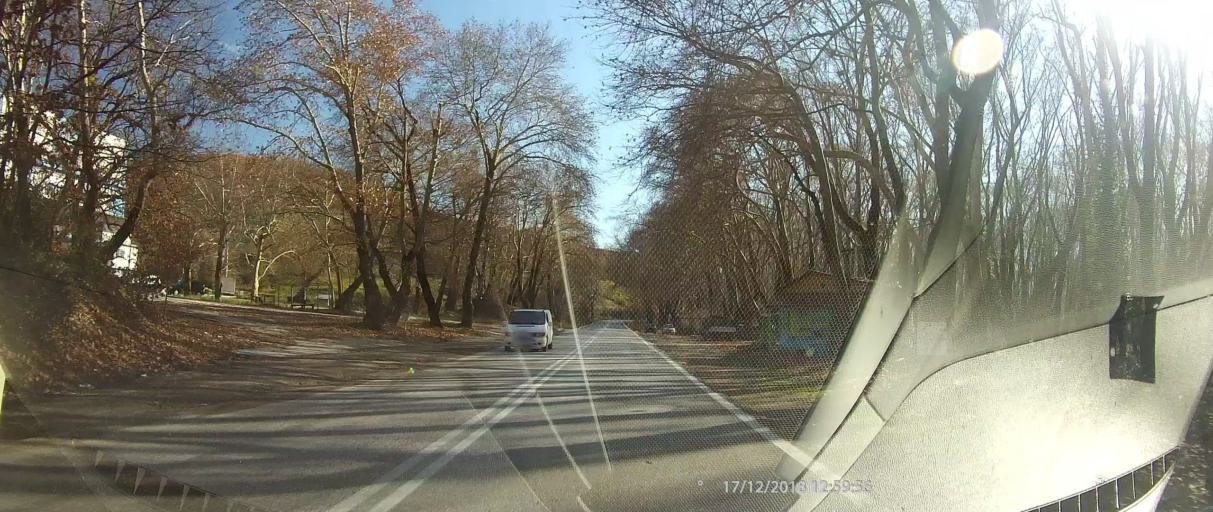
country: GR
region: Thessaly
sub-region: Trikala
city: Kastraki
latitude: 39.7329
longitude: 21.5623
